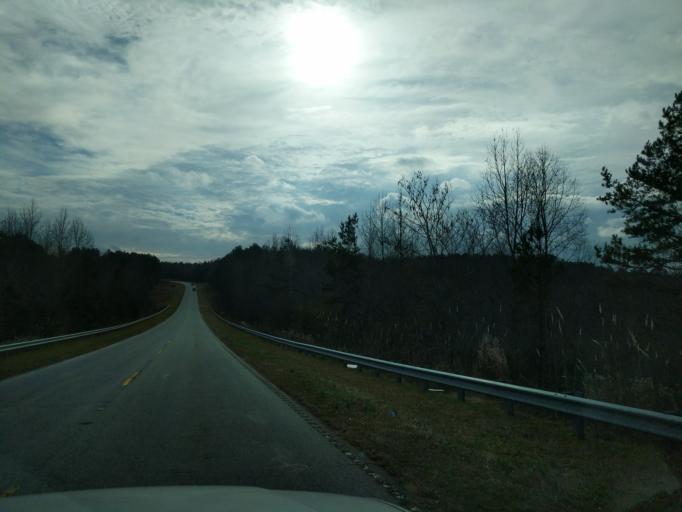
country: US
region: South Carolina
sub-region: Oconee County
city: Westminster
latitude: 34.5857
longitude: -83.0475
